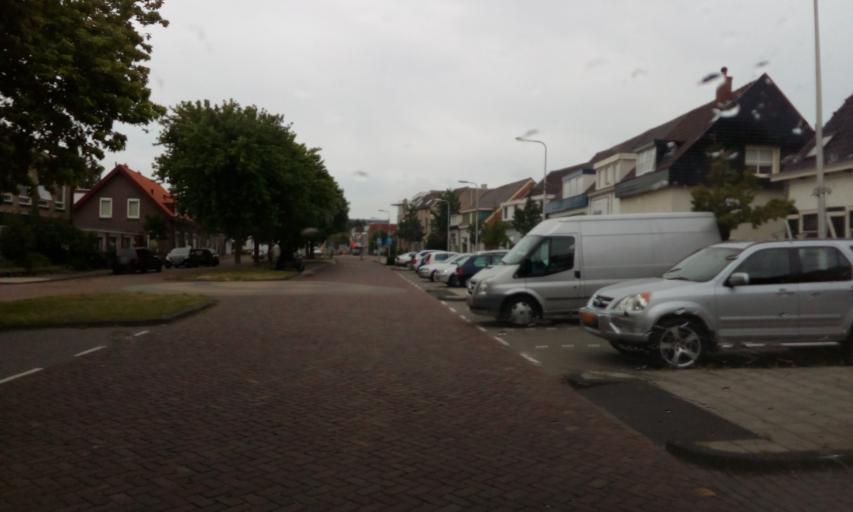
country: NL
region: South Holland
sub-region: Gemeente Westland
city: Honselersdijk
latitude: 52.0098
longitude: 4.2321
